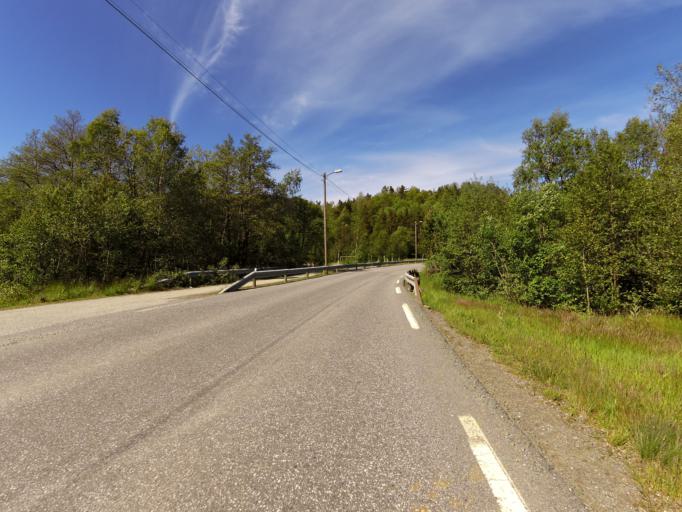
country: NO
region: Hordaland
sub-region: Stord
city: Sagvag
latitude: 59.7870
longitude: 5.4148
